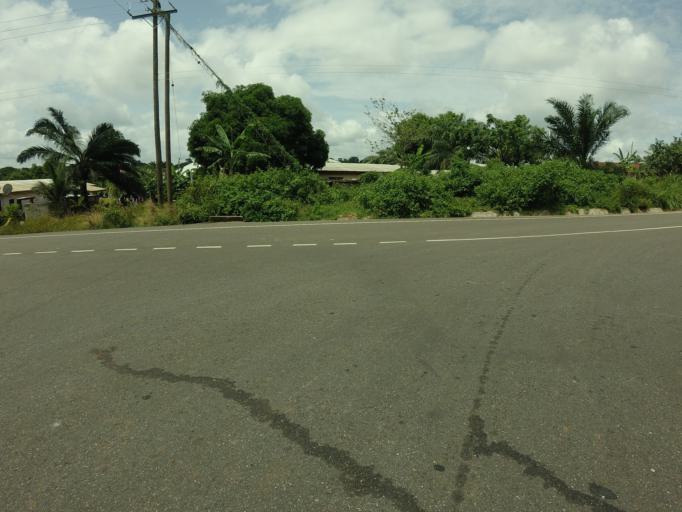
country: GH
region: Volta
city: Ho
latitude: 6.6129
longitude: 0.4577
